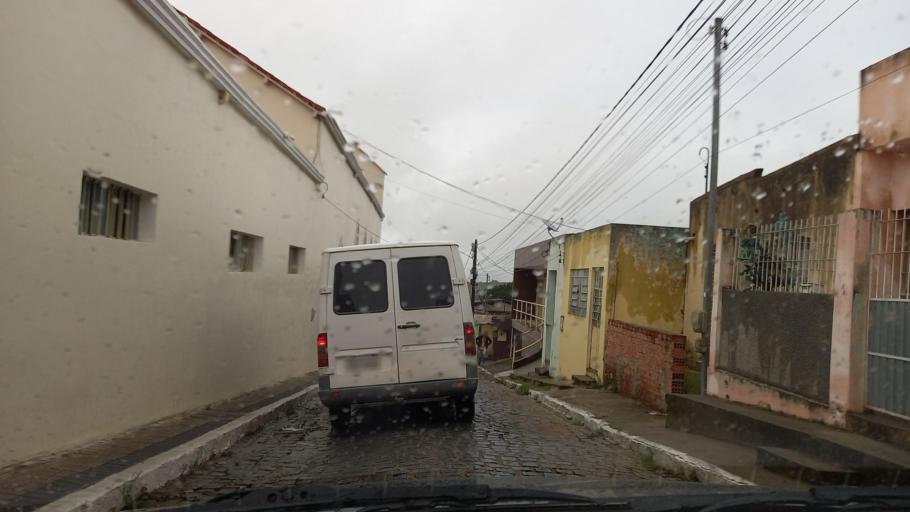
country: BR
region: Pernambuco
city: Garanhuns
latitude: -8.8844
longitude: -36.5009
